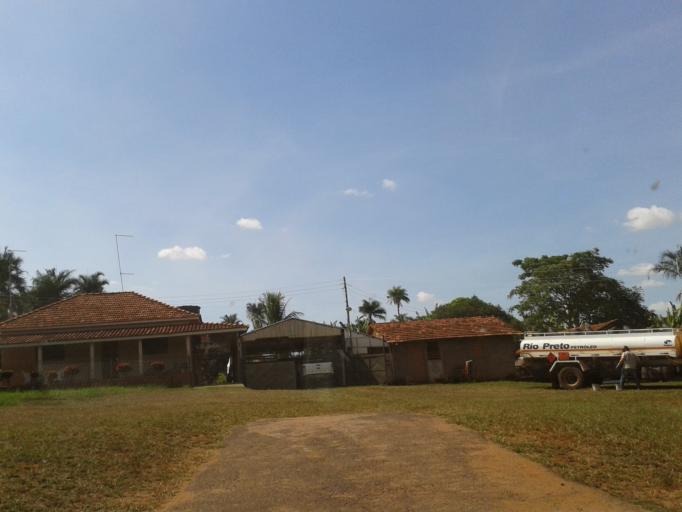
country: BR
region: Minas Gerais
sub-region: Campina Verde
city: Campina Verde
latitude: -19.5222
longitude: -49.5687
